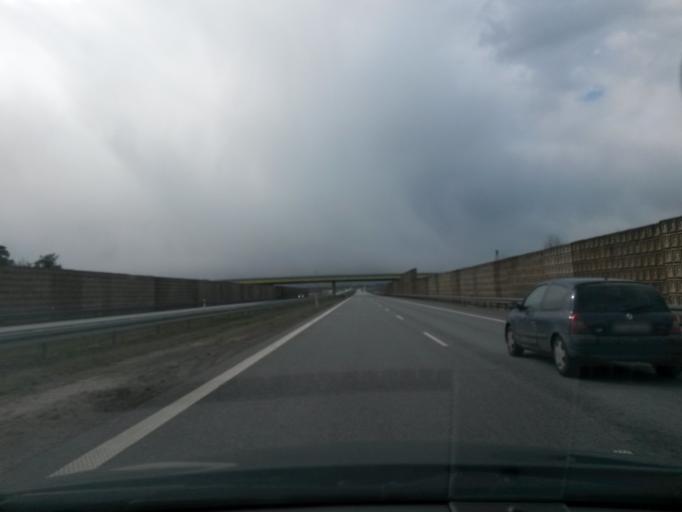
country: PL
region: Greater Poland Voivodeship
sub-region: Powiat koninski
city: Stare Miasto
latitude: 52.1610
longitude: 18.2316
